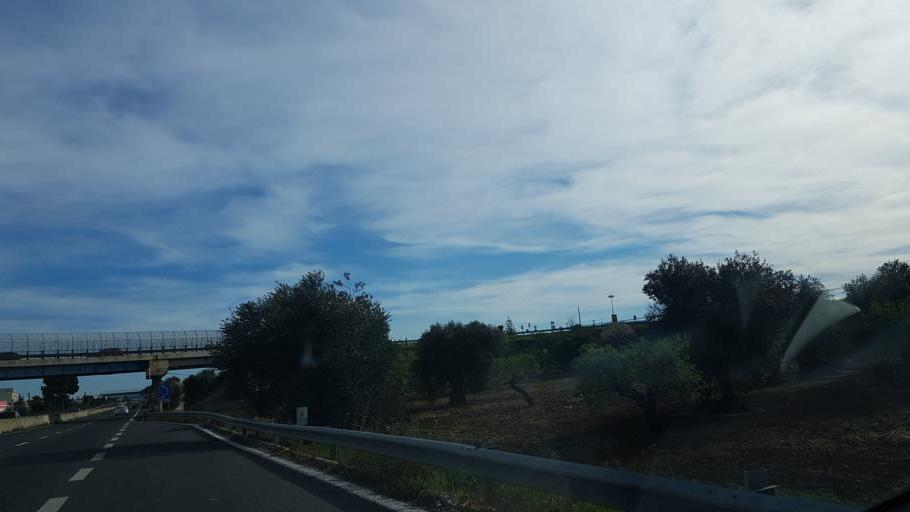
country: IT
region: Apulia
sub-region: Provincia di Bari
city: Monopoli
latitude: 40.8951
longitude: 17.3304
